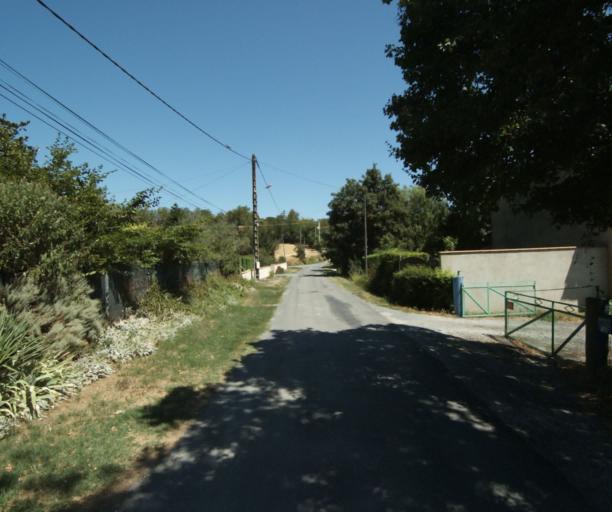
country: FR
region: Midi-Pyrenees
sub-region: Departement de la Haute-Garonne
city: Saint-Felix-Lauragais
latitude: 43.4775
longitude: 1.9199
